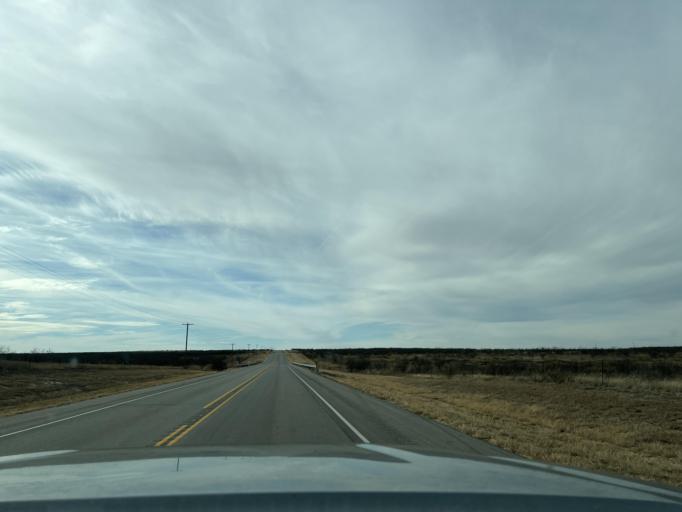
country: US
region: Texas
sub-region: Jones County
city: Anson
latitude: 32.7504
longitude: -99.6546
